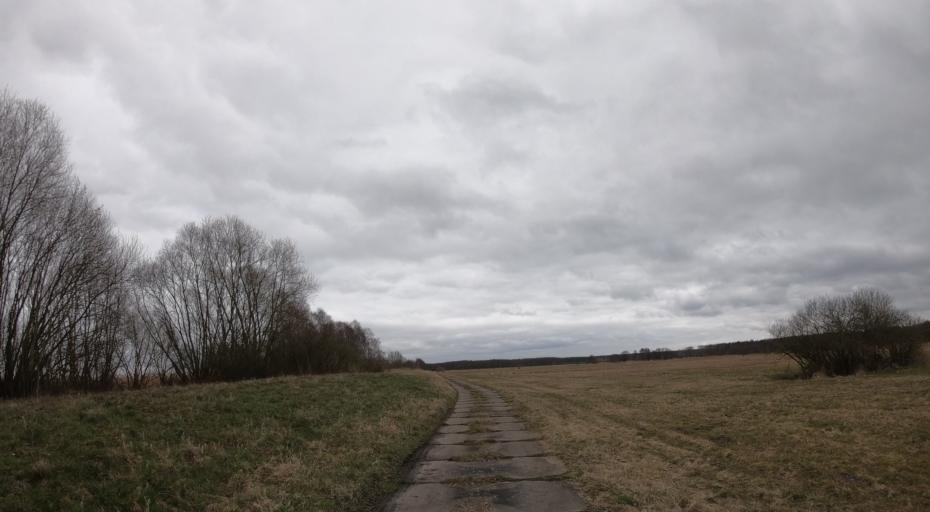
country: PL
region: West Pomeranian Voivodeship
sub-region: Powiat policki
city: Nowe Warpno
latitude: 53.6909
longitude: 14.3828
